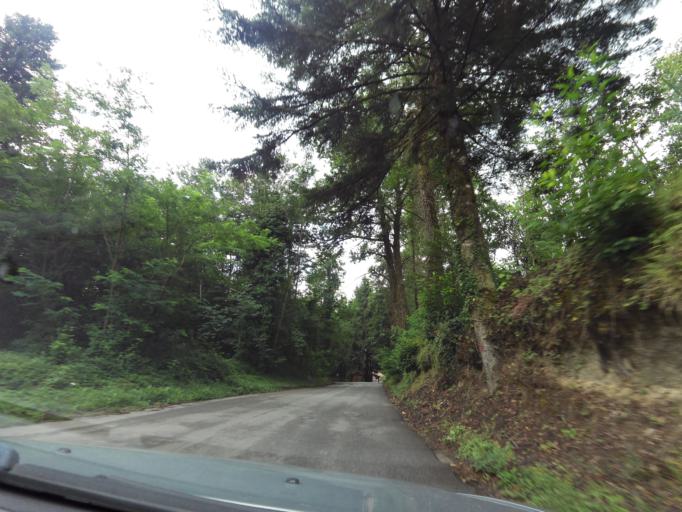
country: IT
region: Calabria
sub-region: Provincia di Vibo-Valentia
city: Serra San Bruno
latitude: 38.5623
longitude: 16.3156
